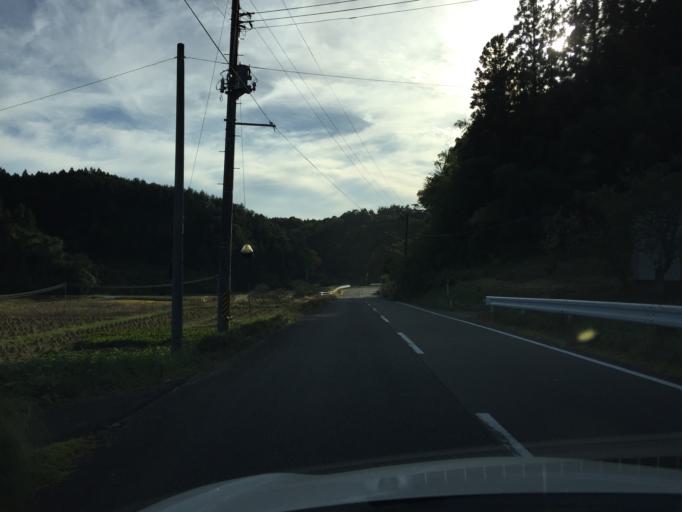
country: JP
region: Fukushima
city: Ishikawa
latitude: 37.2065
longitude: 140.5957
